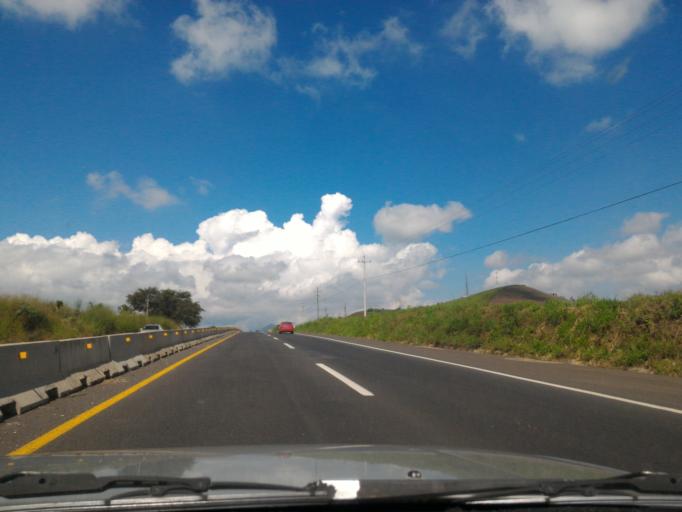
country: MX
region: Jalisco
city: Arenal
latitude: 20.7591
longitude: -103.6665
